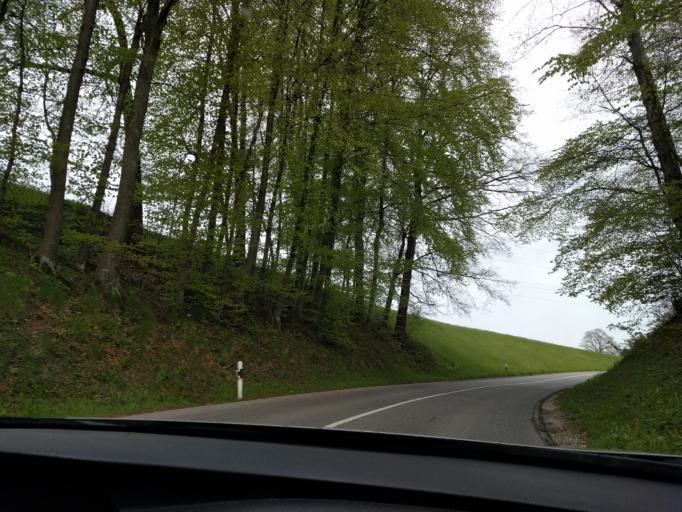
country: CH
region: Fribourg
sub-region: Sense District
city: Schmitten
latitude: 46.8482
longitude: 7.2675
